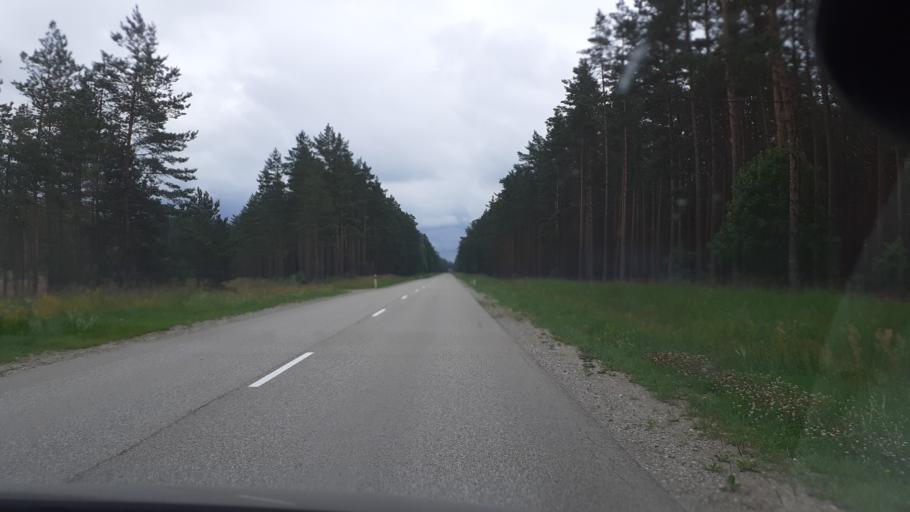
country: LV
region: Ventspils Rajons
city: Piltene
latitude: 57.1144
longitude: 21.7557
